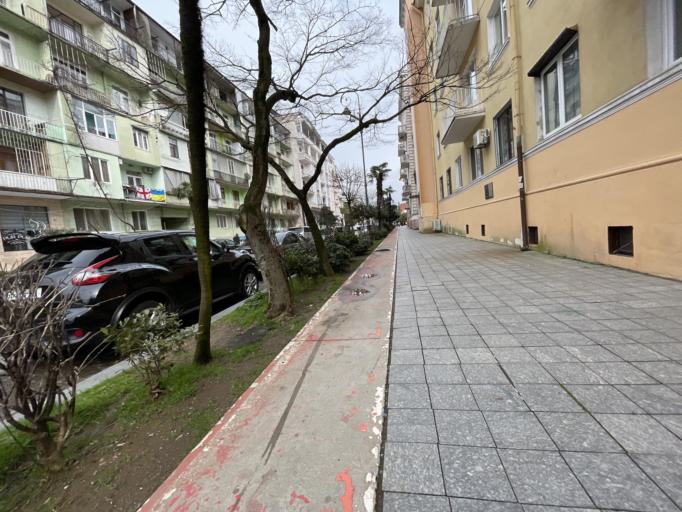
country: GE
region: Ajaria
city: Batumi
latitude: 41.6487
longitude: 41.6316
